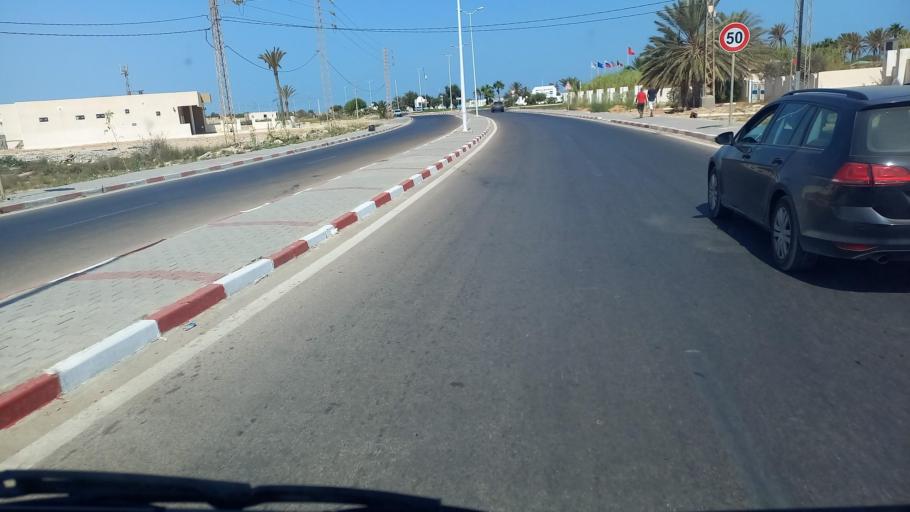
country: TN
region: Madanin
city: Midoun
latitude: 33.8680
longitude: 10.9588
